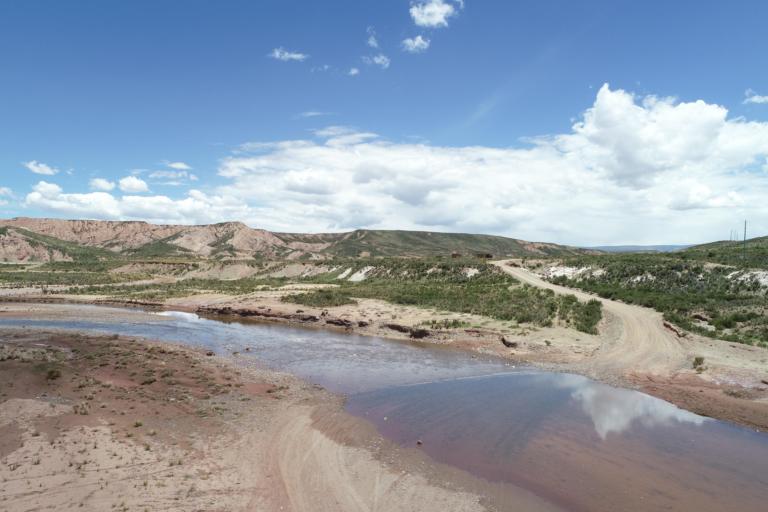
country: BO
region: La Paz
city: Curahuara de Carangas
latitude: -17.3104
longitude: -68.4962
